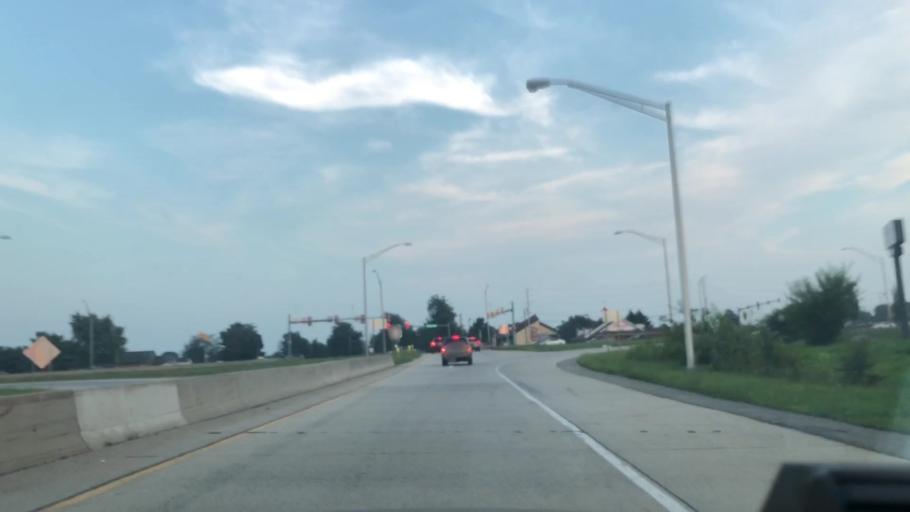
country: US
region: Pennsylvania
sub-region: Lehigh County
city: Fullerton
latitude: 40.6411
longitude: -75.4348
